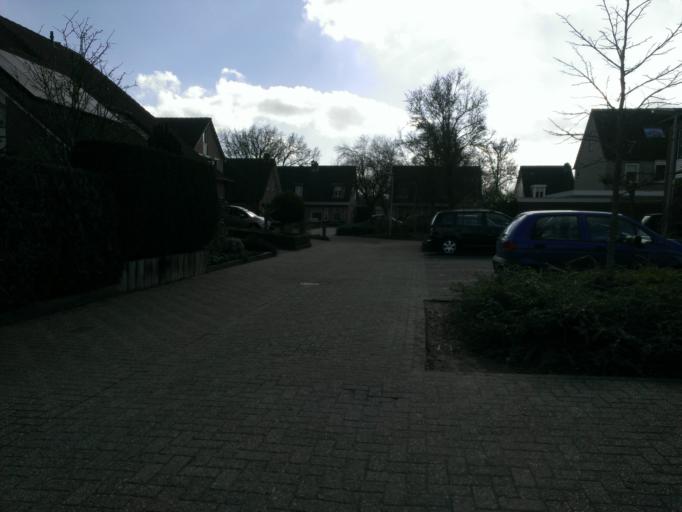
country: NL
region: Gelderland
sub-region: Gemeente Voorst
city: Twello
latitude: 52.2279
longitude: 6.1055
